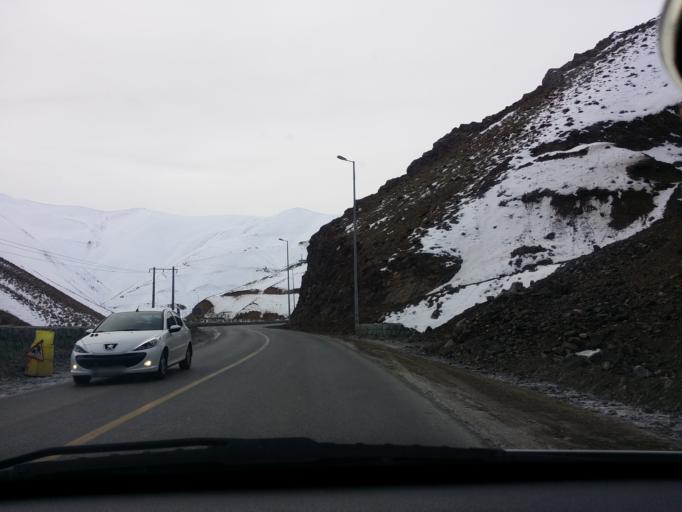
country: IR
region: Tehran
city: Tajrish
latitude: 36.1679
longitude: 51.3163
